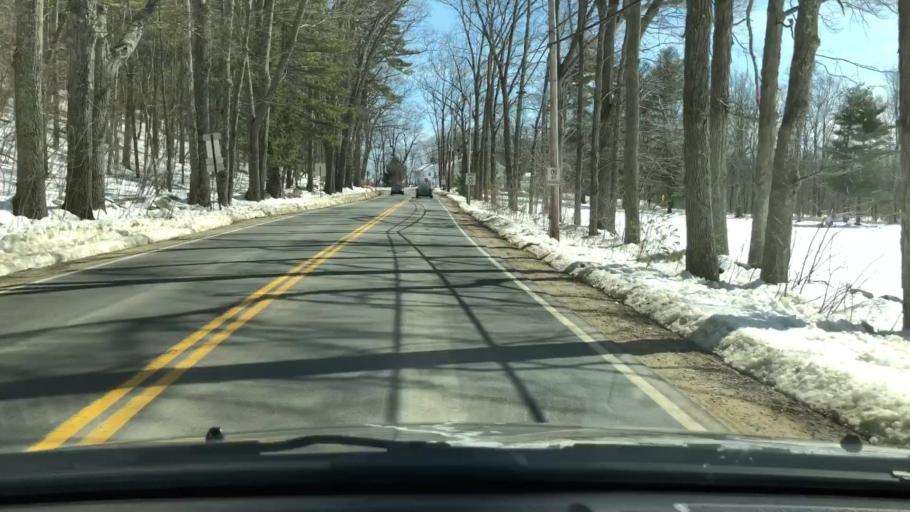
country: US
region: New Hampshire
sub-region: Strafford County
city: Madbury
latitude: 43.1666
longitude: -70.9393
